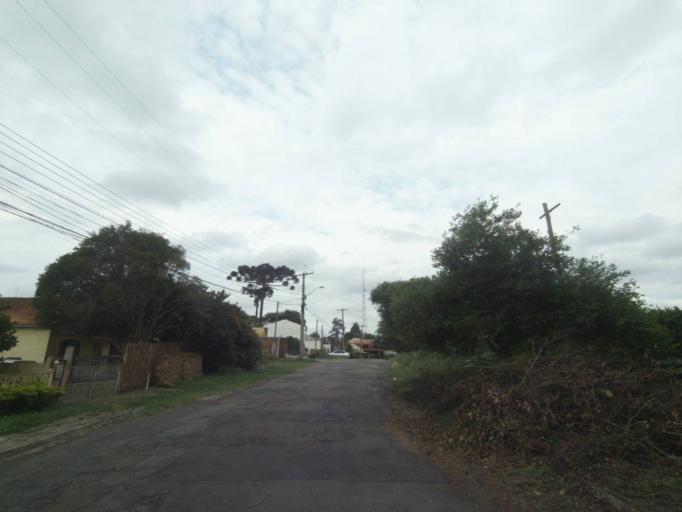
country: BR
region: Parana
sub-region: Curitiba
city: Curitiba
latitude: -25.3996
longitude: -49.2919
